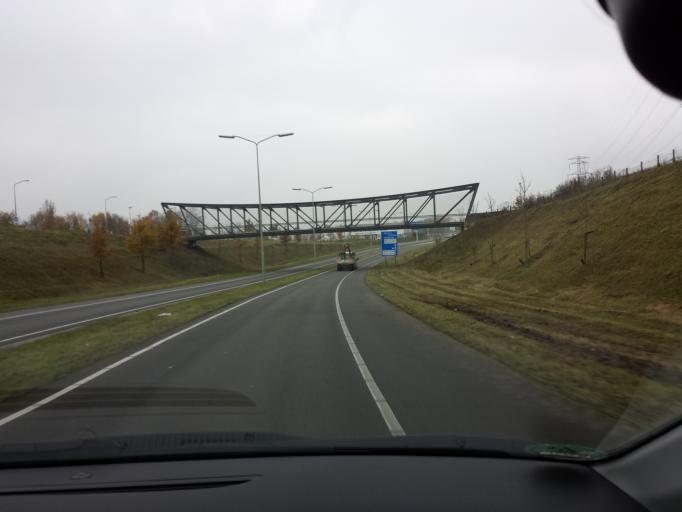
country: NL
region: Limburg
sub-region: Gemeente Heerlen
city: Heerlen
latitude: 50.8771
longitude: 6.0100
